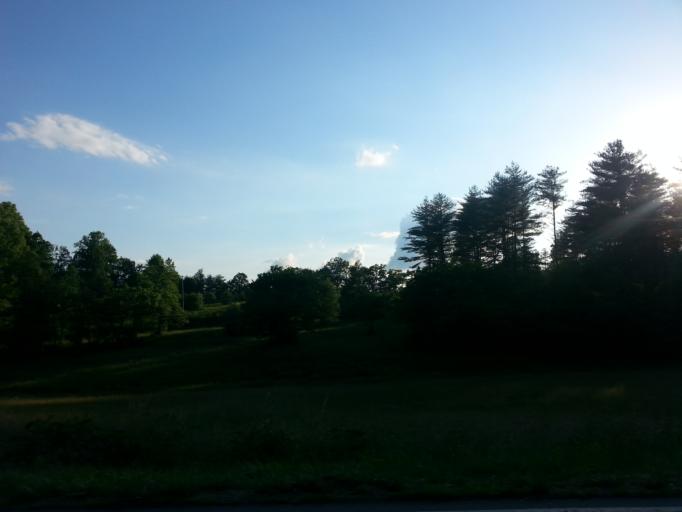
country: US
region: North Carolina
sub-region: Cherokee County
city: Murphy
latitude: 35.0335
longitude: -84.1410
